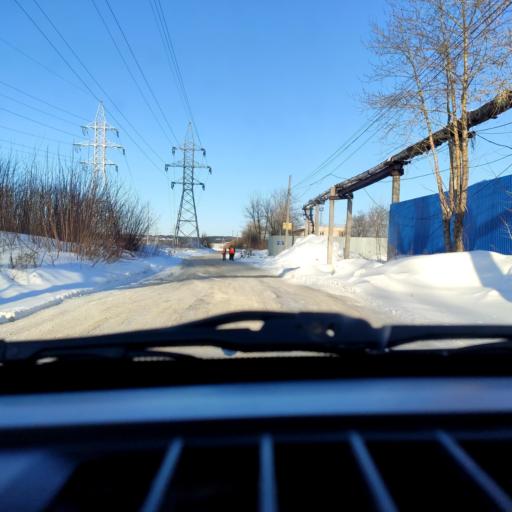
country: RU
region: Perm
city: Kondratovo
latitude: 57.9226
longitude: 56.1550
